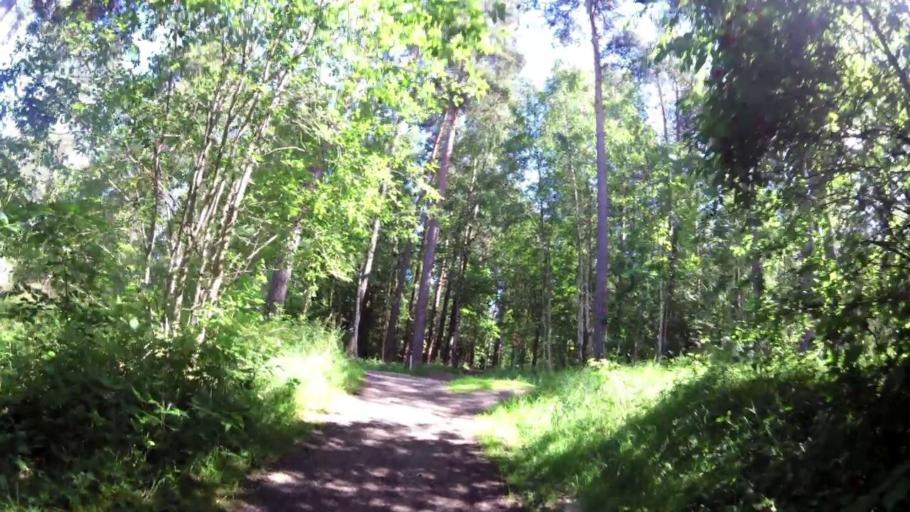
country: SE
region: OEstergoetland
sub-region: Linkopings Kommun
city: Linkoping
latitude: 58.4001
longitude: 15.6004
